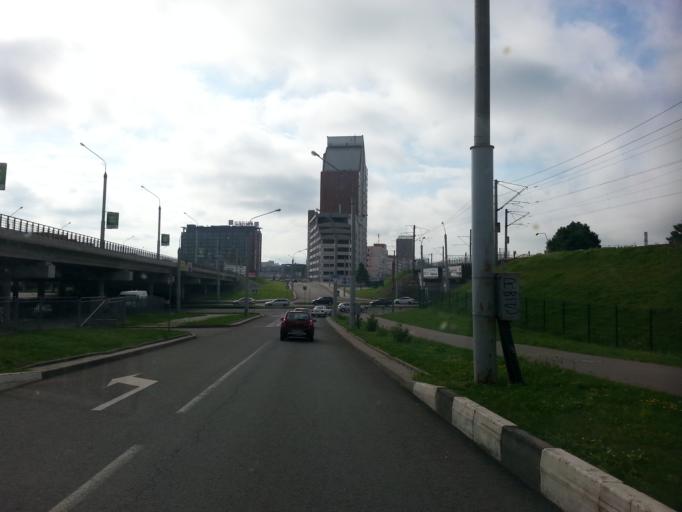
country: BY
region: Minsk
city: Minsk
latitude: 53.9271
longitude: 27.5048
